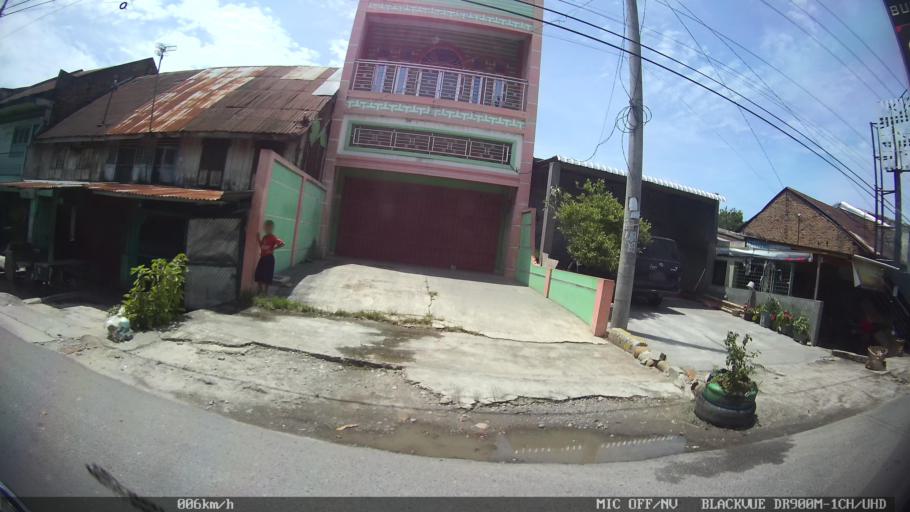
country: ID
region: North Sumatra
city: Percut
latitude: 3.5545
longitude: 98.8804
